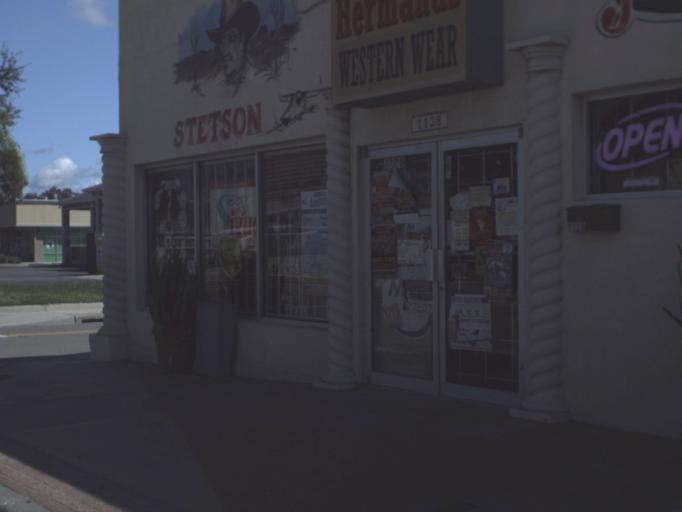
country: US
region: Florida
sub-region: Manatee County
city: Palmetto
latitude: 27.5229
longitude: -82.5729
